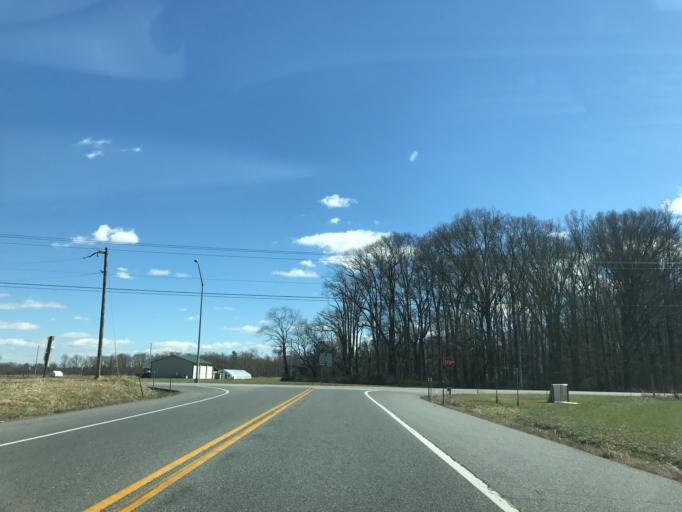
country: US
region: Maryland
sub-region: Queen Anne's County
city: Kingstown
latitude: 39.2398
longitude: -75.8722
